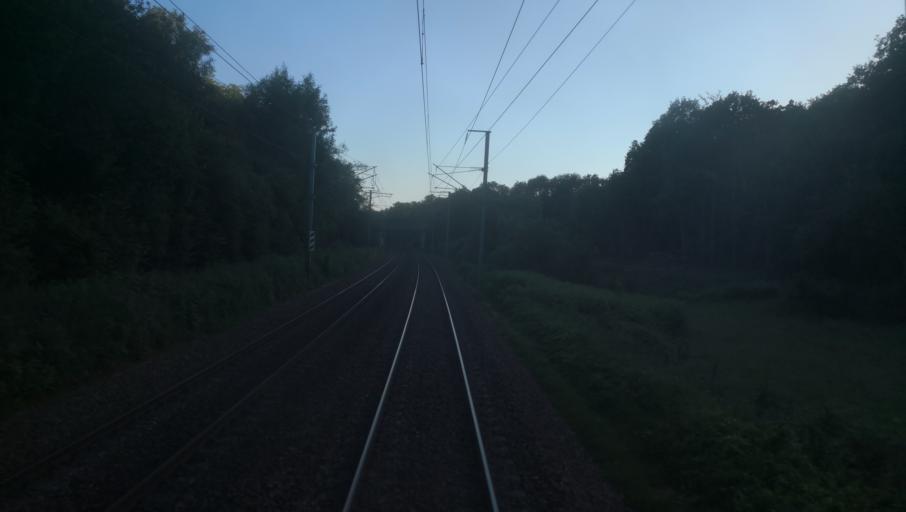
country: FR
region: Haute-Normandie
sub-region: Departement de l'Eure
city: Bernay
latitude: 49.0929
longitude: 0.5337
